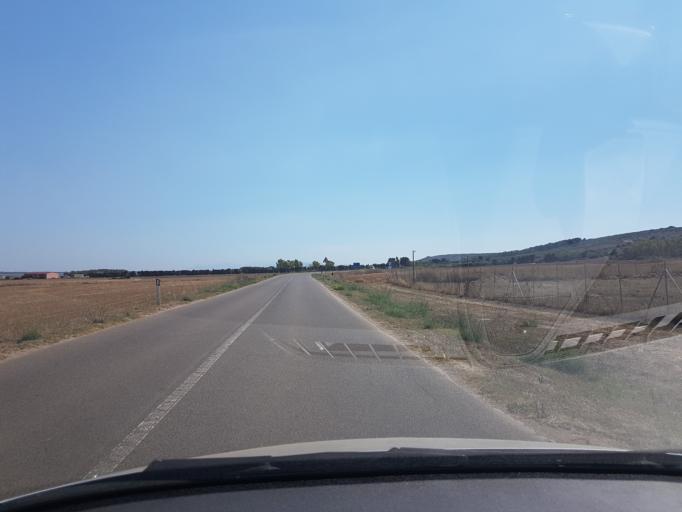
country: IT
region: Sardinia
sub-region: Provincia di Oristano
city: Cabras
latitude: 39.9636
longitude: 8.4536
